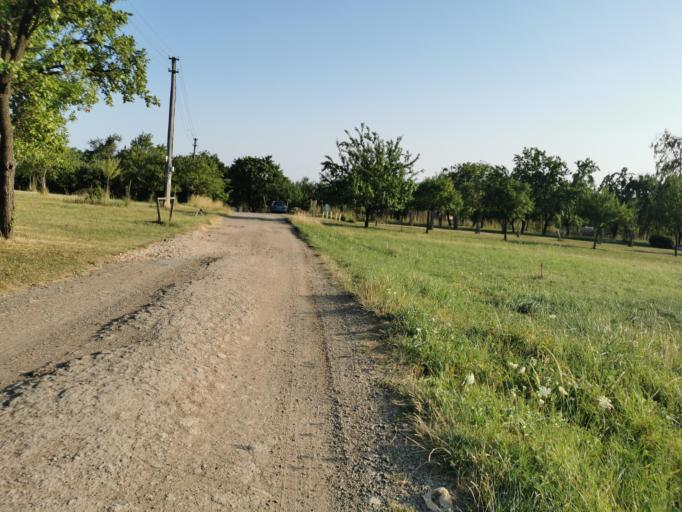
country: CZ
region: South Moravian
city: Sudomerice
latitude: 48.8031
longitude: 17.2919
